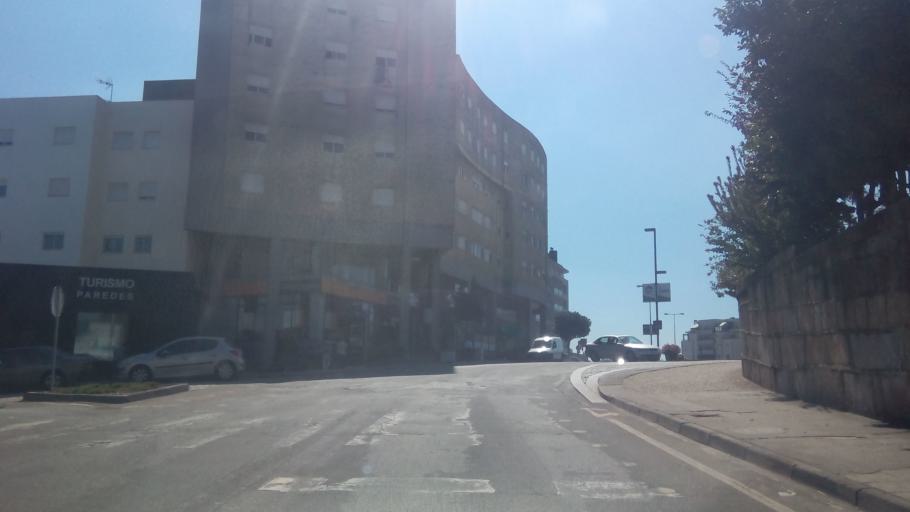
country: PT
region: Porto
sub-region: Paredes
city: Paredes
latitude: 41.2040
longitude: -8.3250
